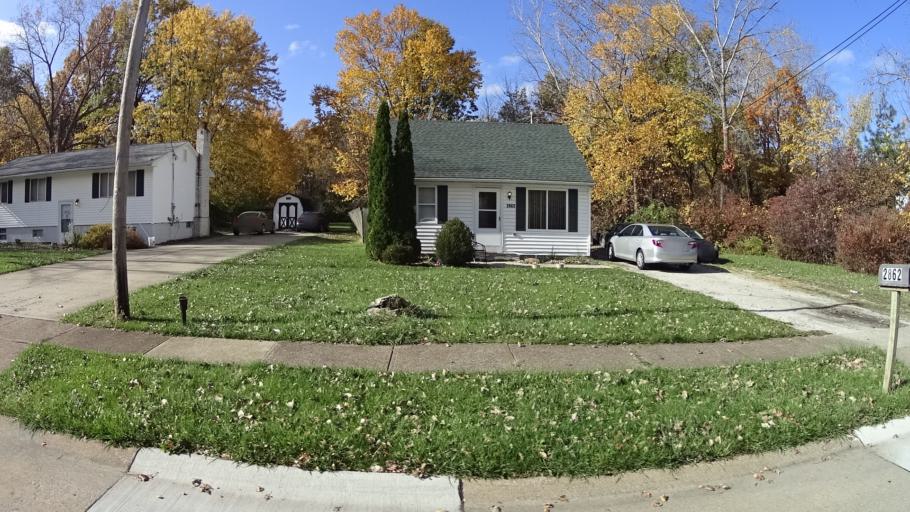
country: US
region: Ohio
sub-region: Lorain County
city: Lorain
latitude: 41.4440
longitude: -82.2242
